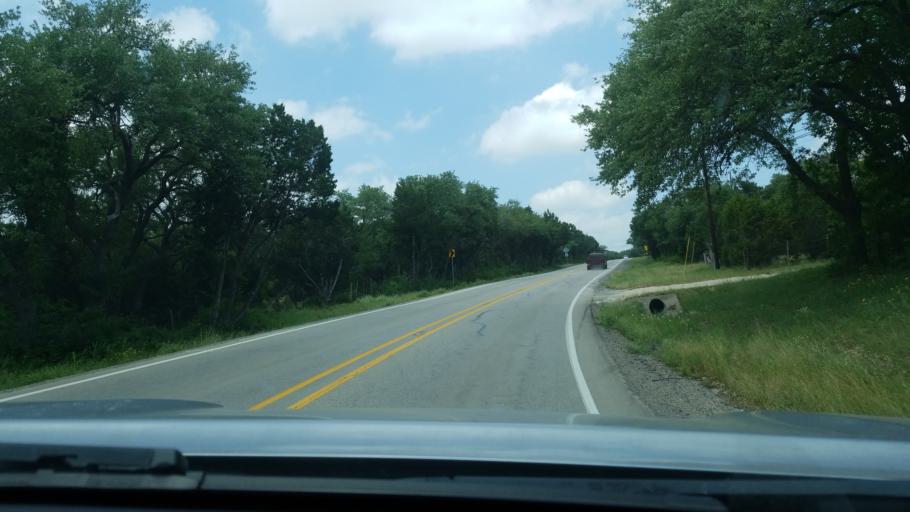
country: US
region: Texas
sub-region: Hays County
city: Dripping Springs
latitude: 30.1549
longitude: -98.0673
